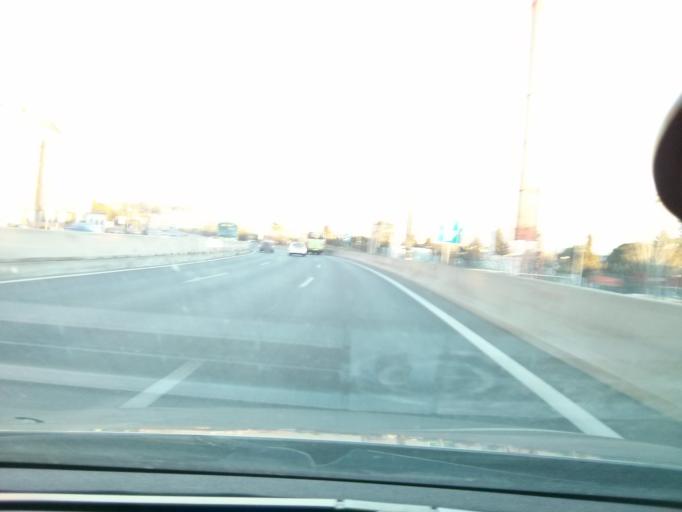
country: ES
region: Madrid
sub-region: Provincia de Madrid
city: Las Rozas de Madrid
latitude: 40.4945
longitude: -3.8686
